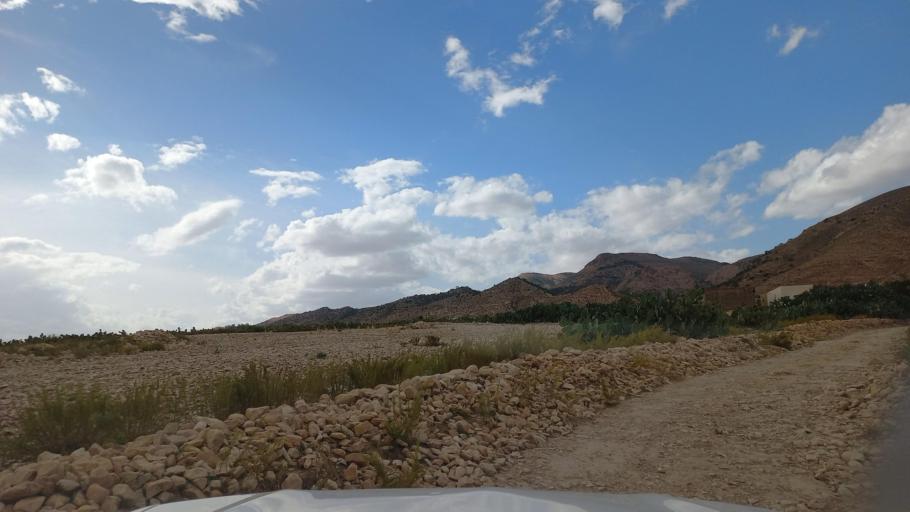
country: TN
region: Al Qasrayn
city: Sbiba
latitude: 35.4496
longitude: 9.0670
